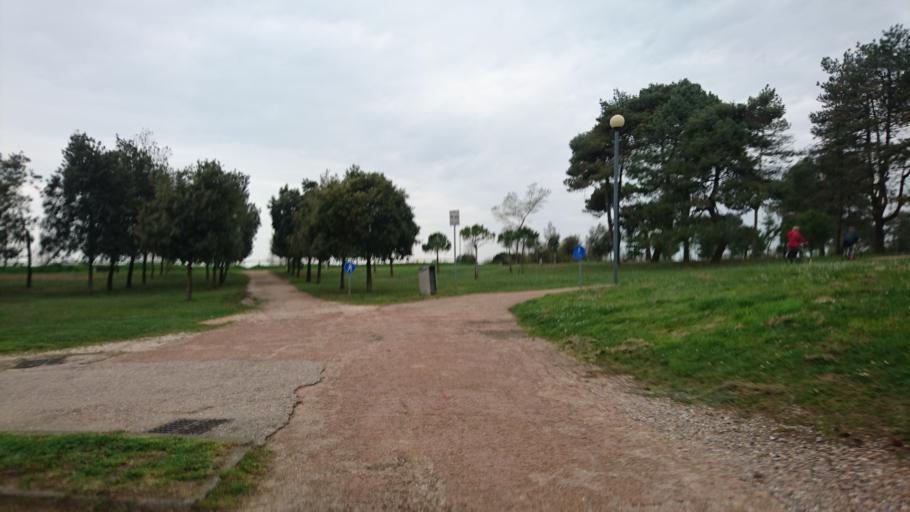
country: IT
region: Veneto
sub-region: Provincia di Venezia
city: Bibione
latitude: 45.6347
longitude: 13.0721
